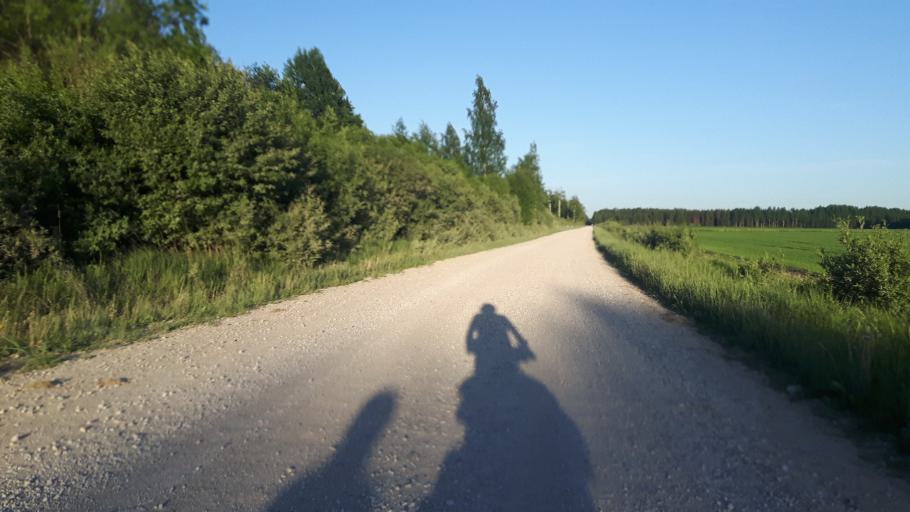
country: EE
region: Raplamaa
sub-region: Jaervakandi vald
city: Jarvakandi
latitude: 58.7565
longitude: 24.9510
